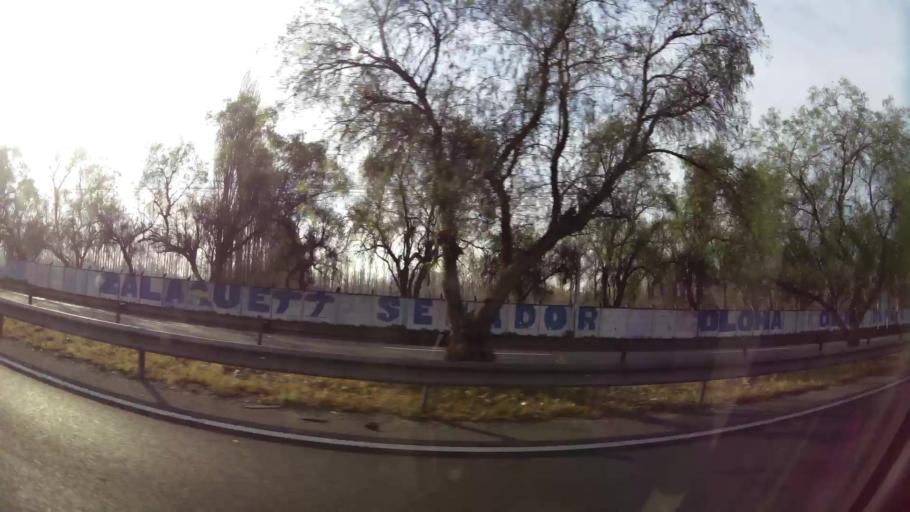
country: CL
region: Santiago Metropolitan
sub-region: Provincia de Talagante
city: Penaflor
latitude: -33.6275
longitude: -70.8642
